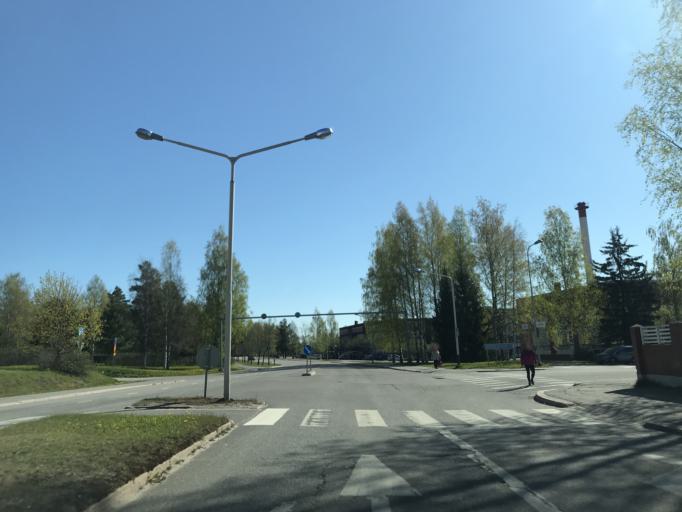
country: FI
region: Paijanne Tavastia
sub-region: Lahti
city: Orimattila
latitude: 60.8059
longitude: 25.7326
